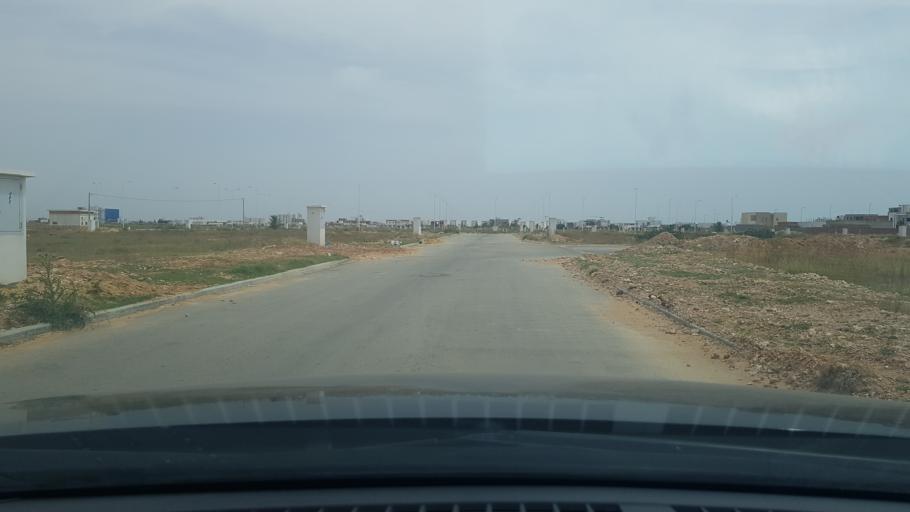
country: TN
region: Safaqis
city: Al Qarmadah
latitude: 34.8261
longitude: 10.7444
